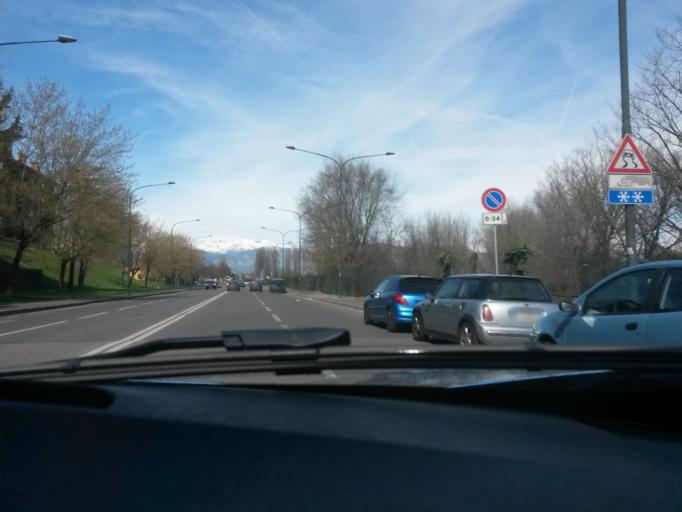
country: IT
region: Piedmont
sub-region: Provincia di Torino
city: Savonera
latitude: 45.0856
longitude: 7.6306
